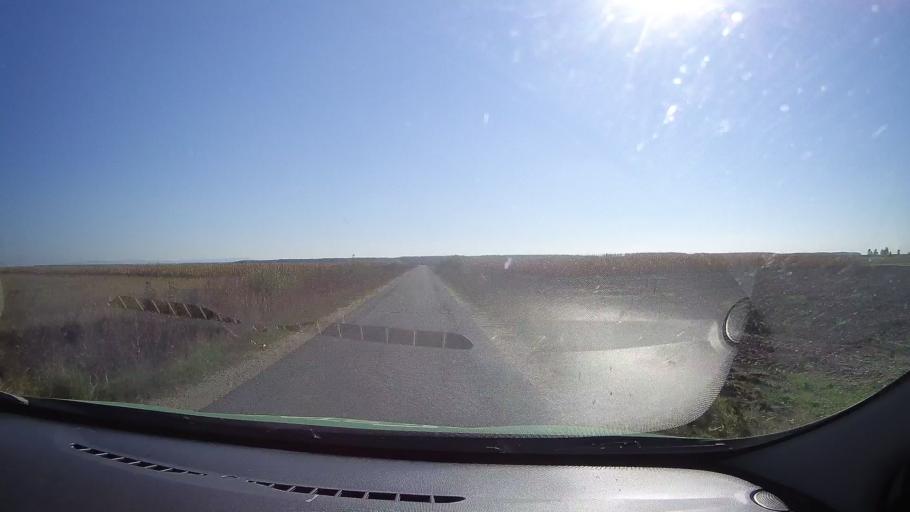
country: RO
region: Satu Mare
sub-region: Comuna Doba
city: Doba
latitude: 47.7345
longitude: 22.7219
